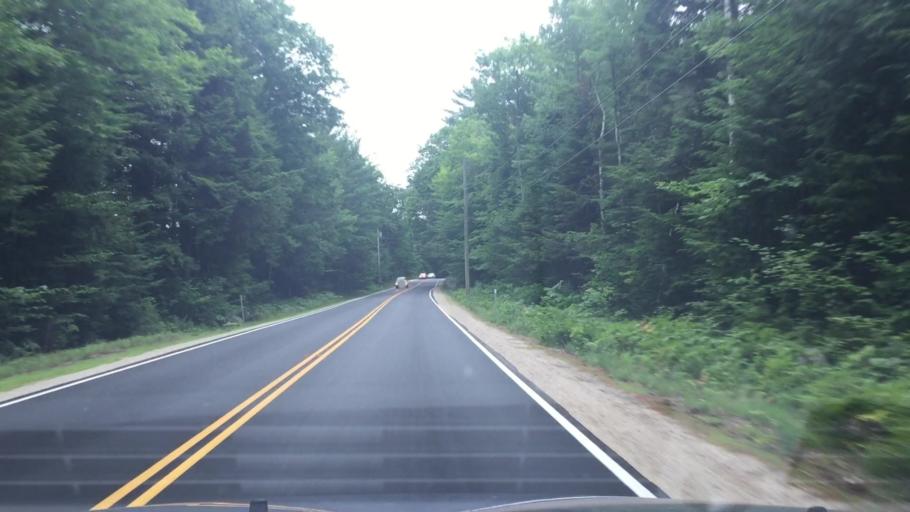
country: US
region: New Hampshire
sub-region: Carroll County
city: Freedom
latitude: 43.8391
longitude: -71.0798
